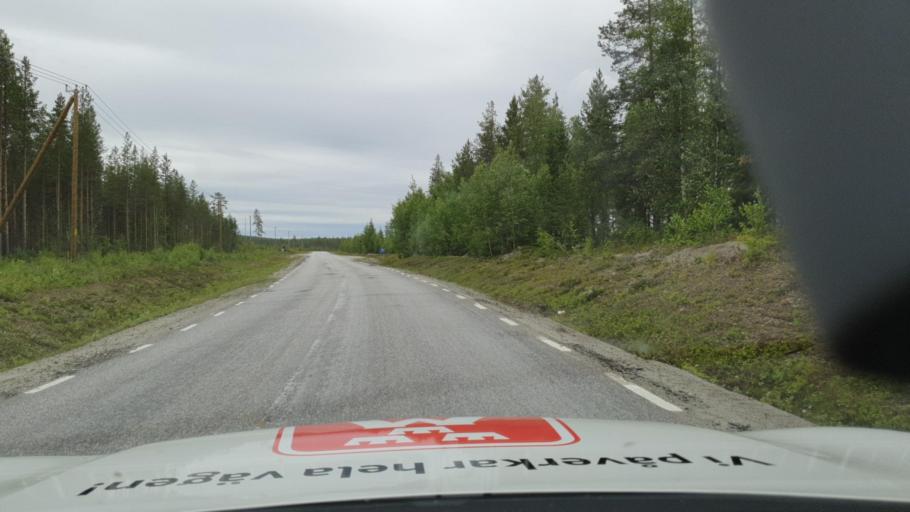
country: SE
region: Vaesterbotten
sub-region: Lycksele Kommun
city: Lycksele
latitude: 64.1198
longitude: 18.3598
